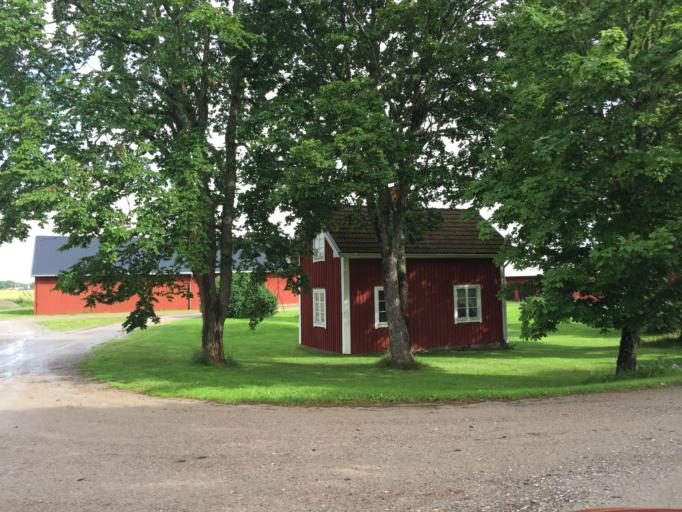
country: SE
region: Soedermanland
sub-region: Vingakers Kommun
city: Vingaker
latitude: 59.0668
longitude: 15.8308
